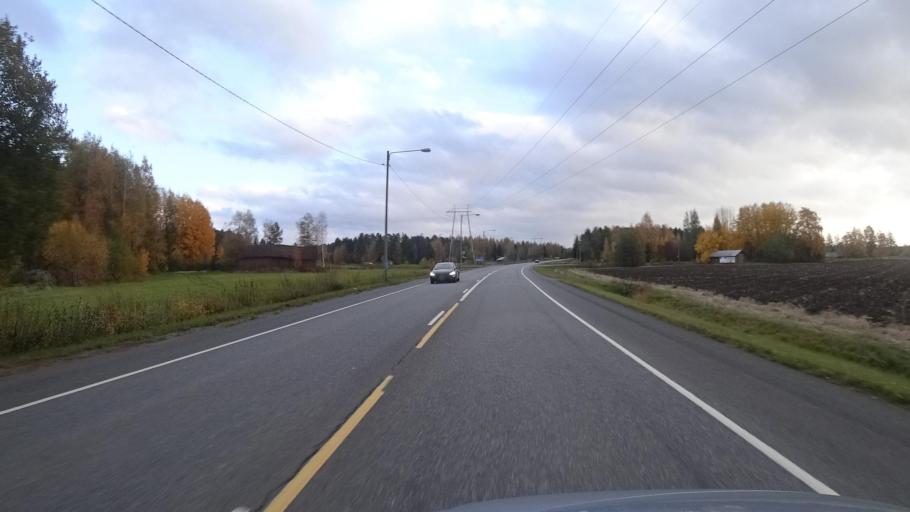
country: FI
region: Satakunta
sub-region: Rauma
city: Saekylae
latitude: 61.0229
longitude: 22.4072
